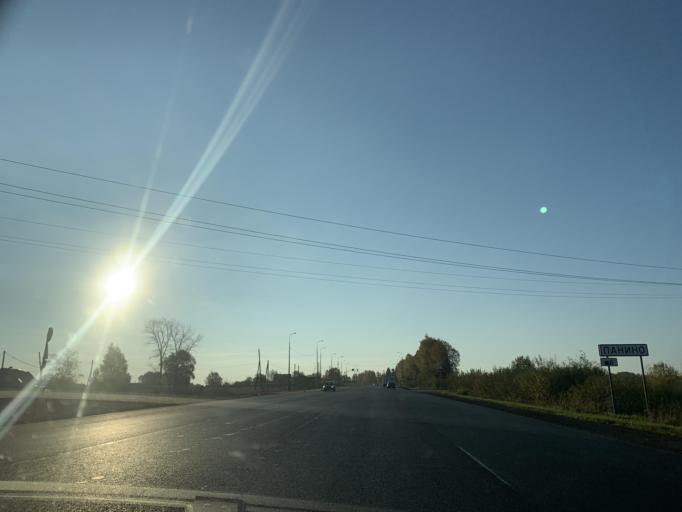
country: RU
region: Jaroslavl
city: Konstantinovskiy
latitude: 57.7912
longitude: 39.6068
